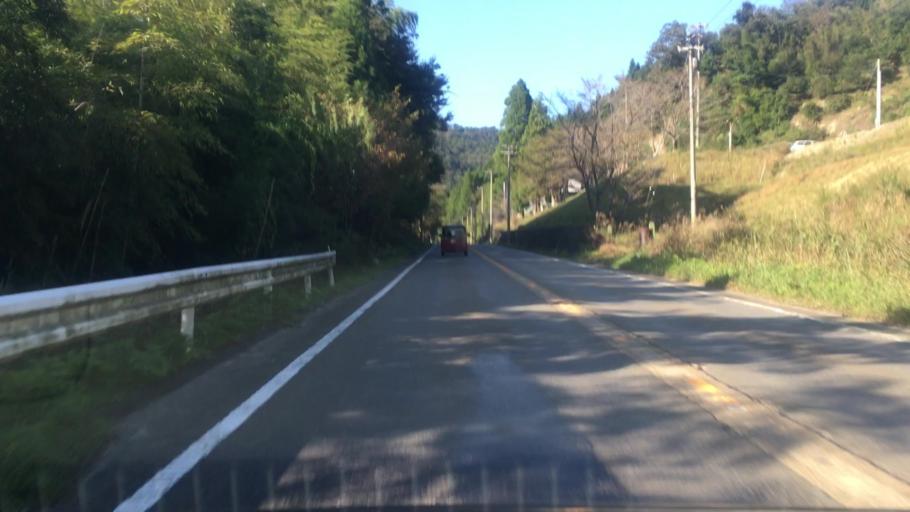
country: JP
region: Hyogo
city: Toyooka
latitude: 35.5665
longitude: 134.8528
